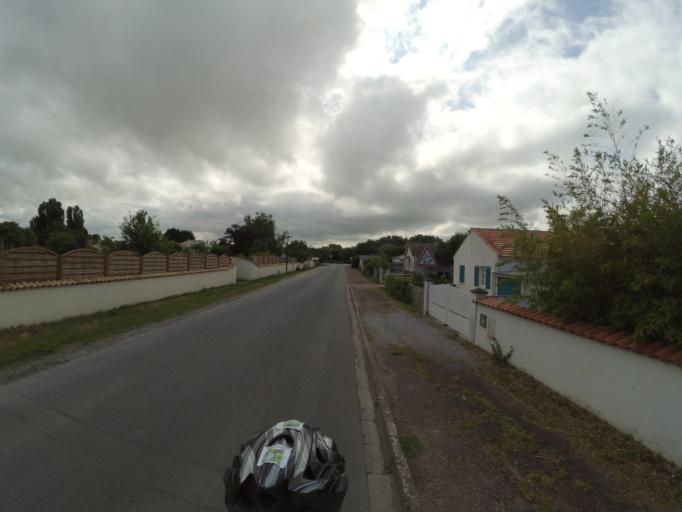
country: FR
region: Poitou-Charentes
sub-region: Departement de la Charente-Maritime
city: Chatelaillon-Plage
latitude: 46.0572
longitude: -1.0778
